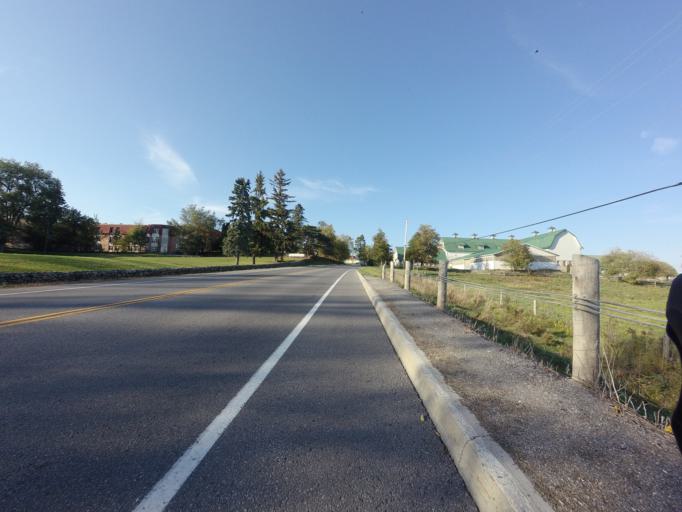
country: CA
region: Ontario
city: Kingston
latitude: 44.3119
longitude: -76.4646
